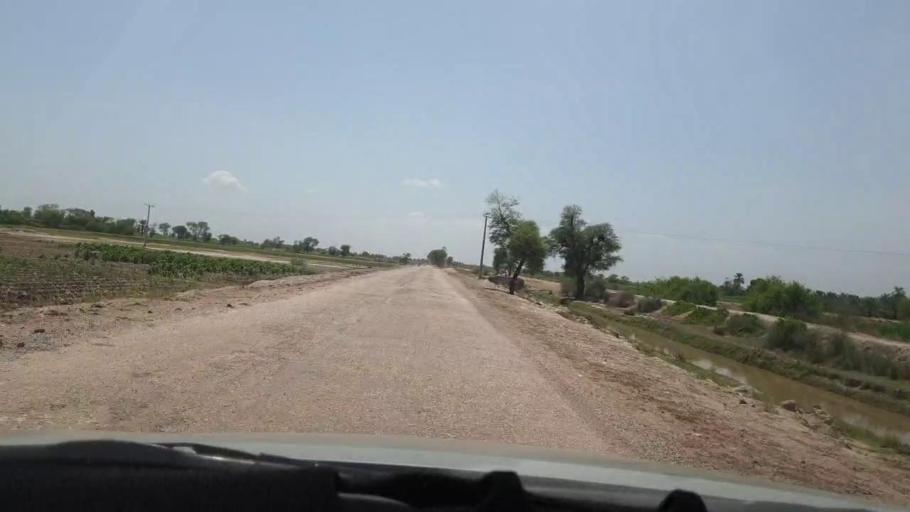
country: PK
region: Sindh
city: Pano Aqil
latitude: 27.7299
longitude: 69.1842
